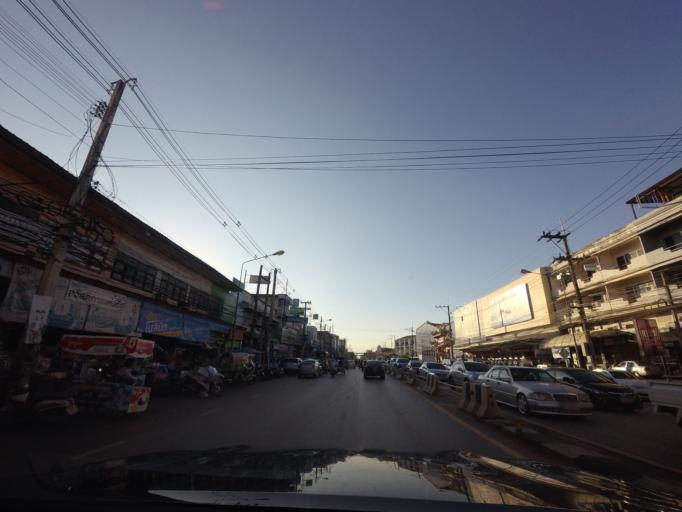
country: TH
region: Changwat Udon Thani
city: Udon Thani
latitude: 17.3970
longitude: 102.8074
